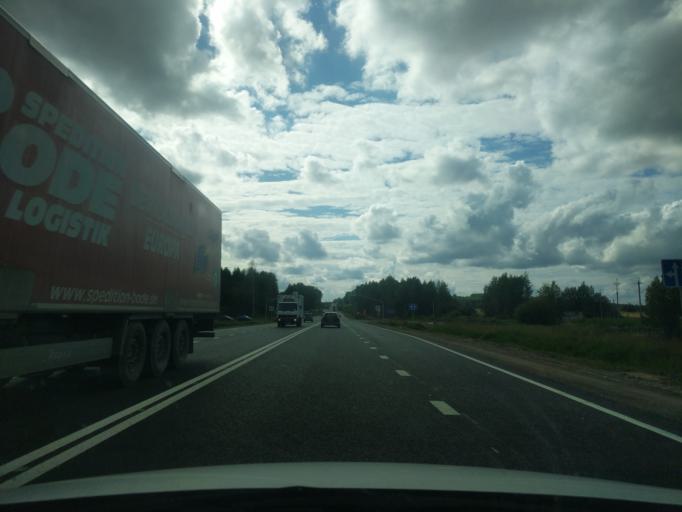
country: RU
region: Kostroma
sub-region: Kostromskoy Rayon
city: Kostroma
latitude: 57.7322
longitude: 40.8185
